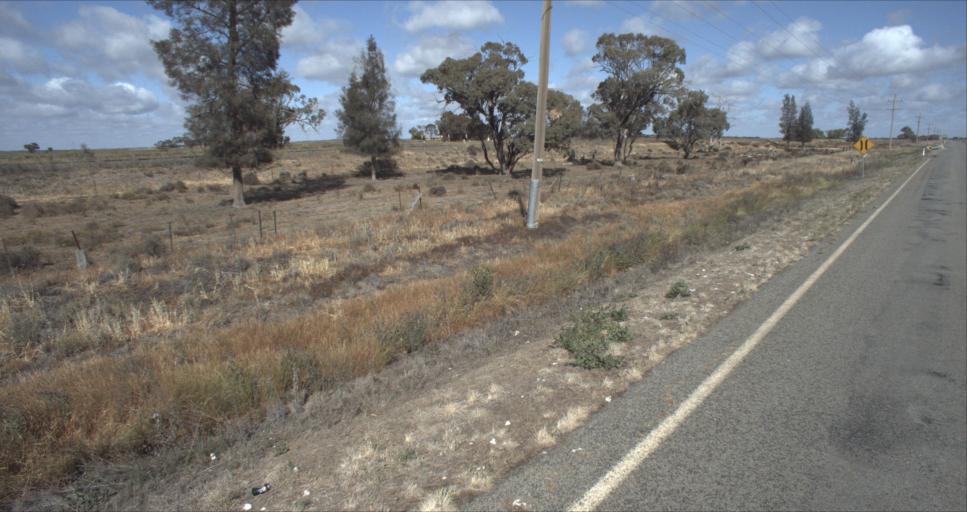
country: AU
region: New South Wales
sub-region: Leeton
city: Leeton
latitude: -34.5365
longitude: 146.2348
